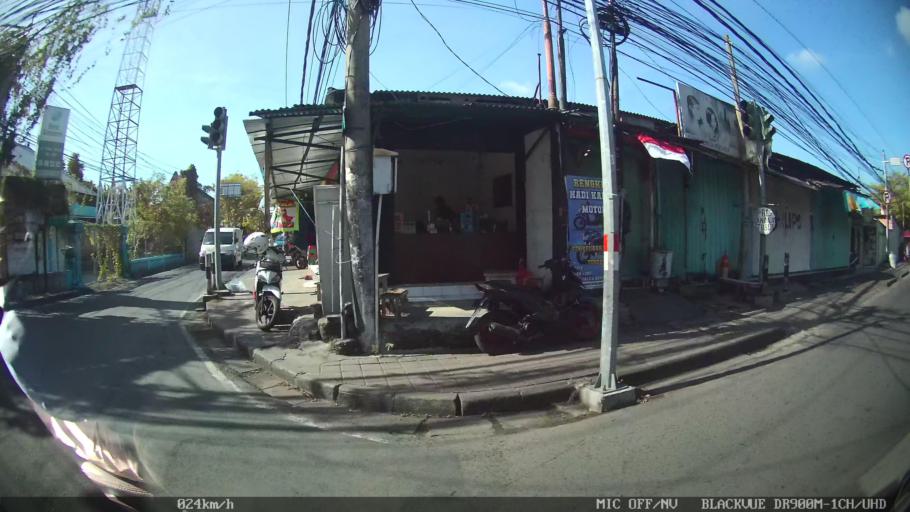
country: ID
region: Bali
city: Jabajero
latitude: -8.7375
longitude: 115.1687
